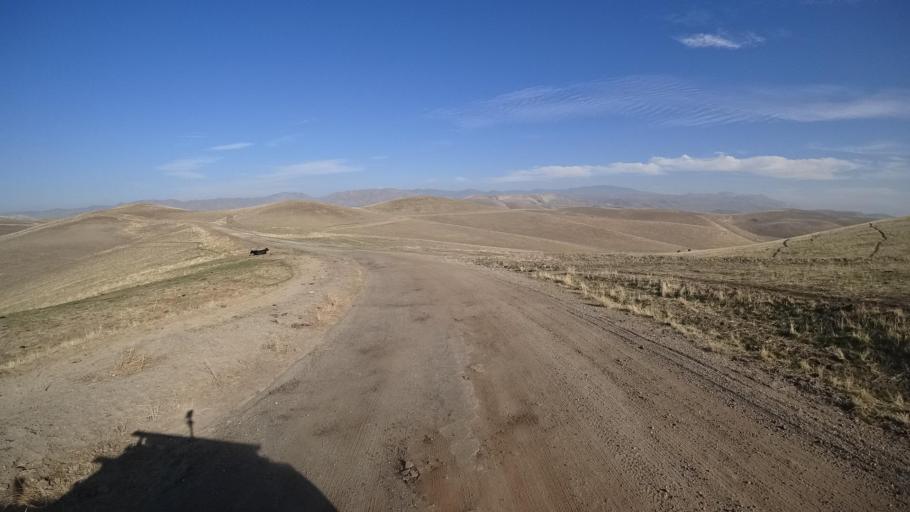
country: US
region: California
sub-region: Kern County
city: Oildale
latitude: 35.4906
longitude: -118.8754
